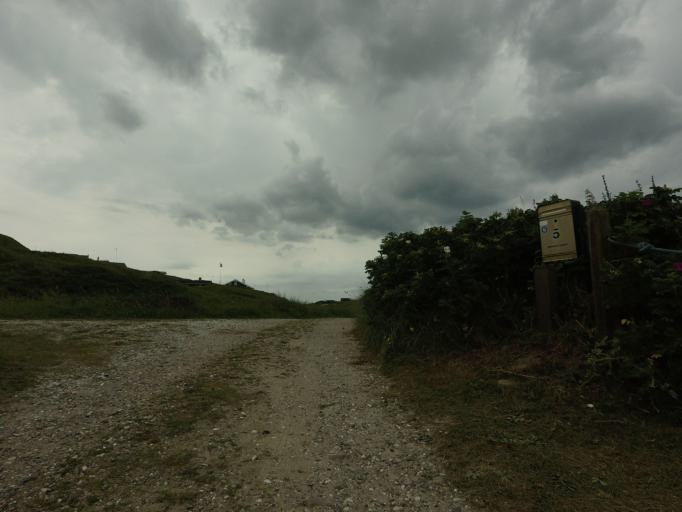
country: DK
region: North Denmark
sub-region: Jammerbugt Kommune
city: Pandrup
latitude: 57.3121
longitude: 9.6505
